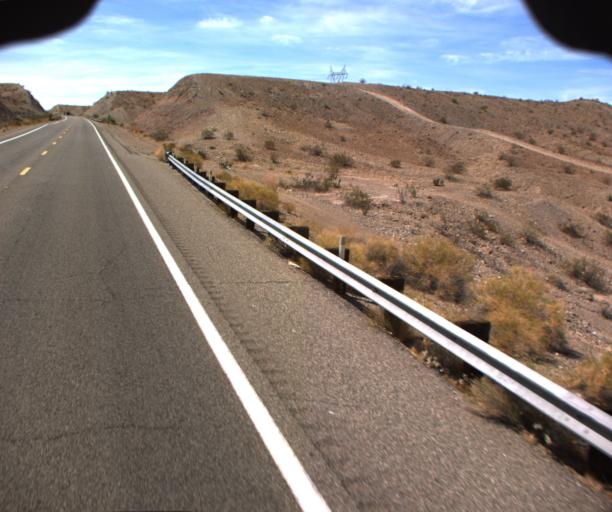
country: US
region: Arizona
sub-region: Mohave County
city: Lake Havasu City
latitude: 34.4244
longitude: -114.2054
